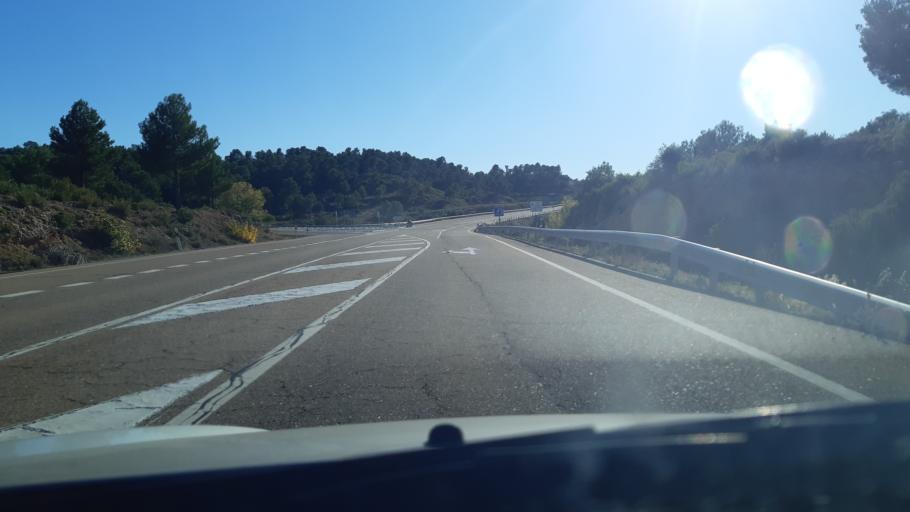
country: ES
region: Aragon
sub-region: Provincia de Teruel
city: Fornoles
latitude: 40.9155
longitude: -0.0203
